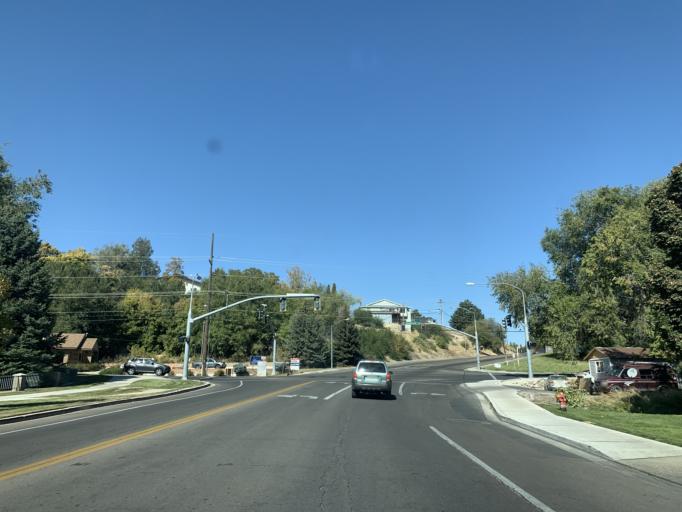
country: US
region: Utah
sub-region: Utah County
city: Provo
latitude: 40.2541
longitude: -111.6737
